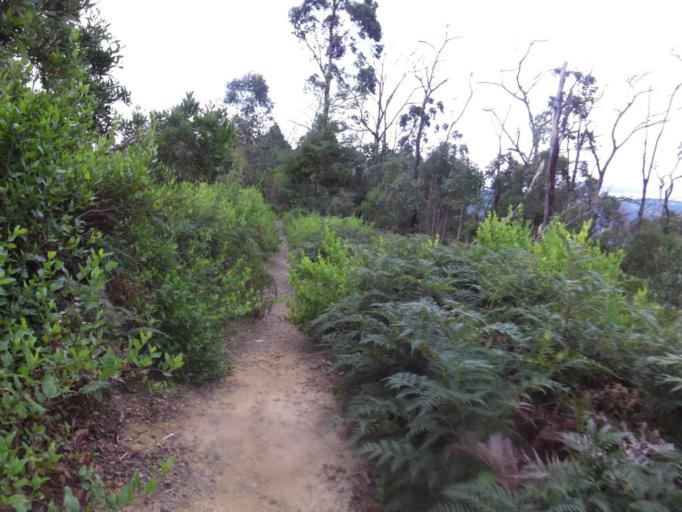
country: AU
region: Victoria
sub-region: Murrindindi
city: Kinglake West
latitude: -37.5274
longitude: 145.2458
